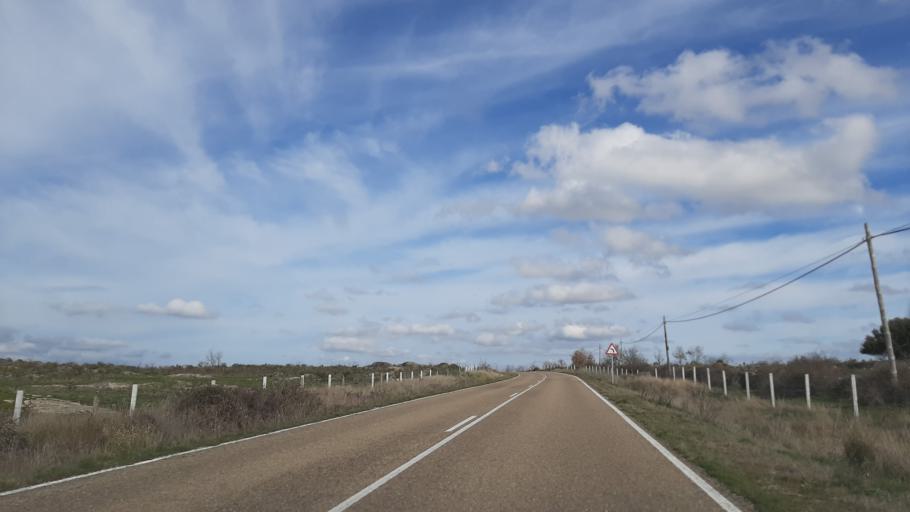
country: ES
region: Castille and Leon
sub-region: Provincia de Salamanca
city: Villarino de los Aires
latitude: 41.2446
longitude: -6.5040
